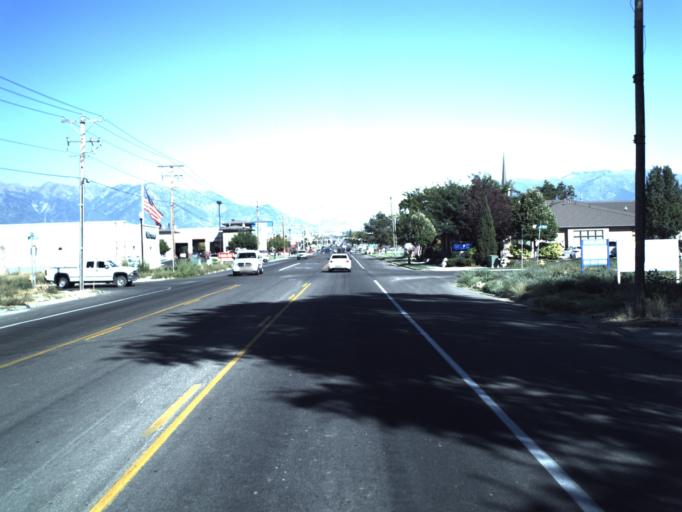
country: US
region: Utah
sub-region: Davis County
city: Clinton
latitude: 41.1398
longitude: -112.0696
